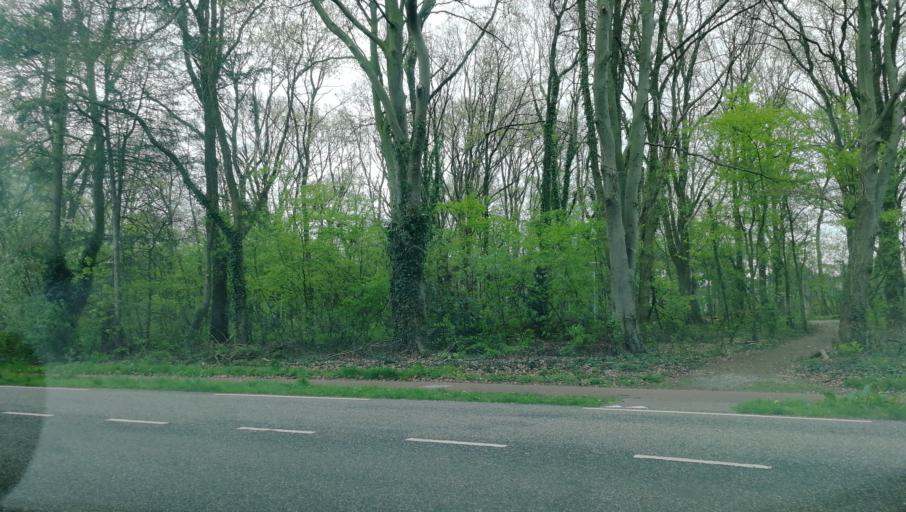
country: NL
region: Limburg
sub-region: Gemeente Venlo
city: Venlo
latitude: 51.3791
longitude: 6.2082
